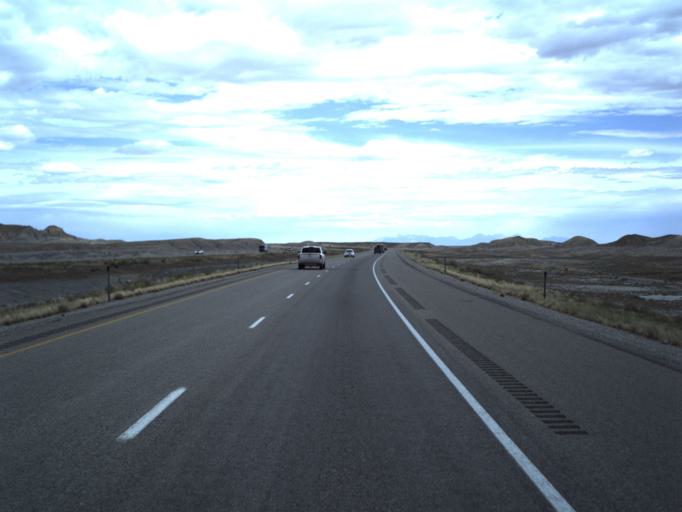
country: US
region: Utah
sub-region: Grand County
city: Moab
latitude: 38.9312
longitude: -110.0145
